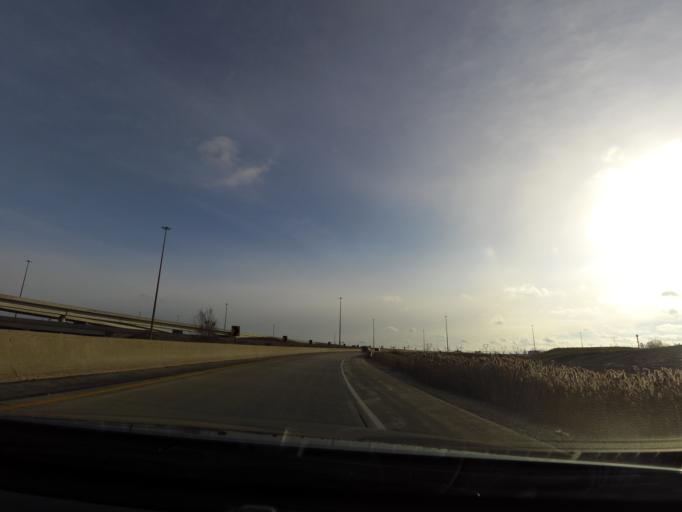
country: CA
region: Ontario
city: Brampton
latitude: 43.6696
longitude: -79.7024
